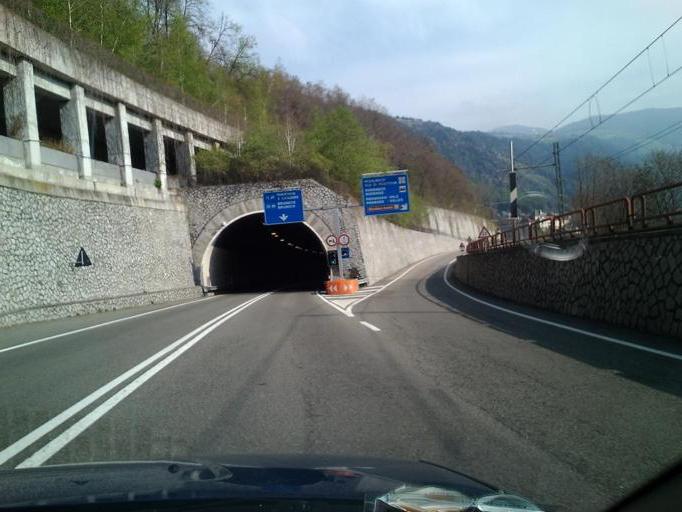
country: IT
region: Trentino-Alto Adige
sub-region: Bolzano
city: Rio di Pusteria
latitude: 46.7905
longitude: 11.6655
